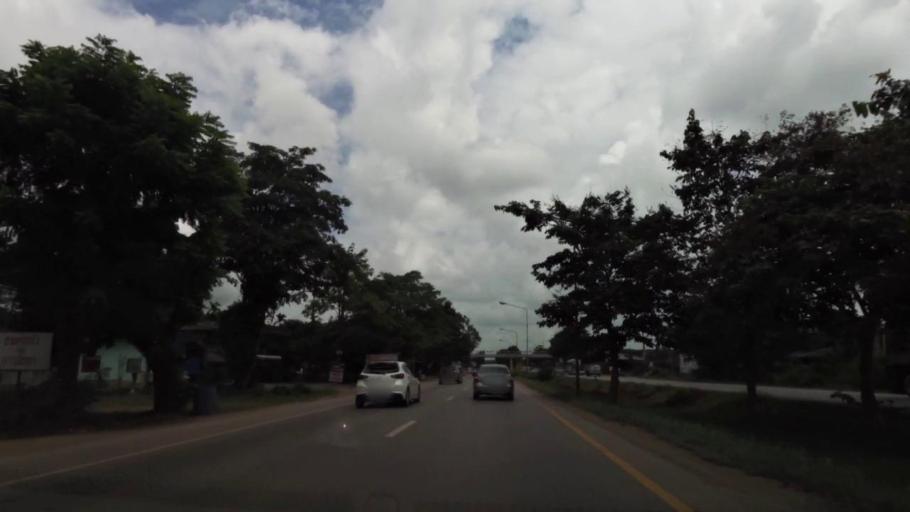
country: TH
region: Chanthaburi
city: Na Yai Am
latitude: 12.7842
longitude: 101.7956
